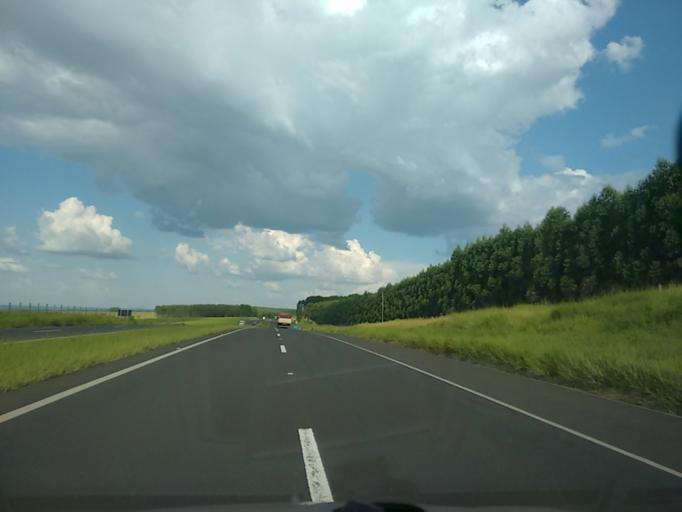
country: BR
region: Sao Paulo
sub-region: Duartina
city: Duartina
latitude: -22.3245
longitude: -49.4088
